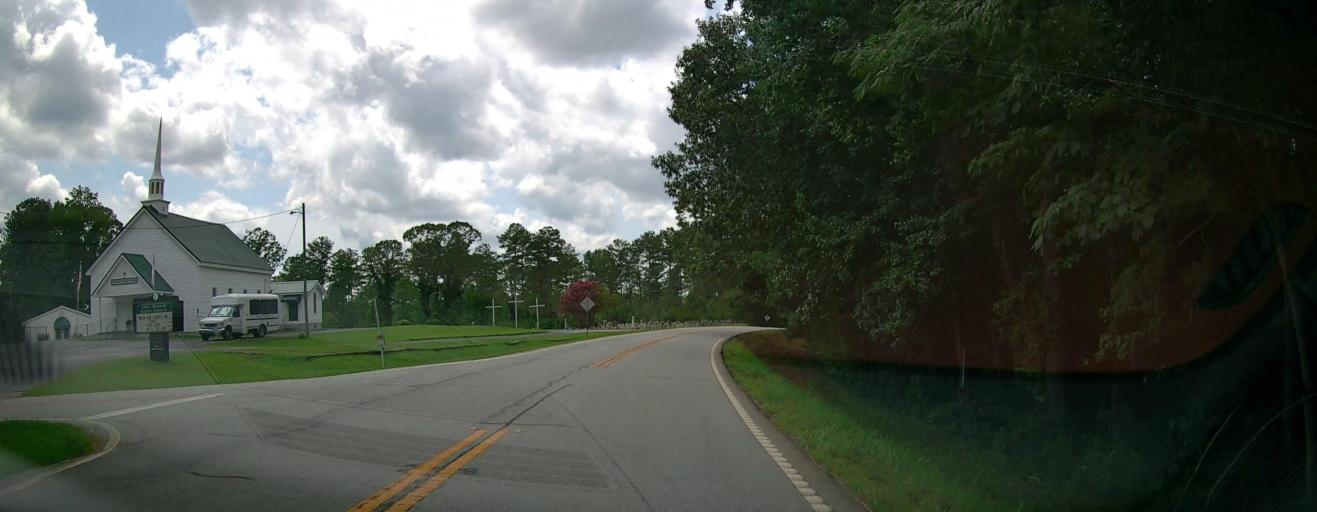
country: US
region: Georgia
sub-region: Heard County
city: Franklin
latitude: 33.3013
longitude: -85.1349
